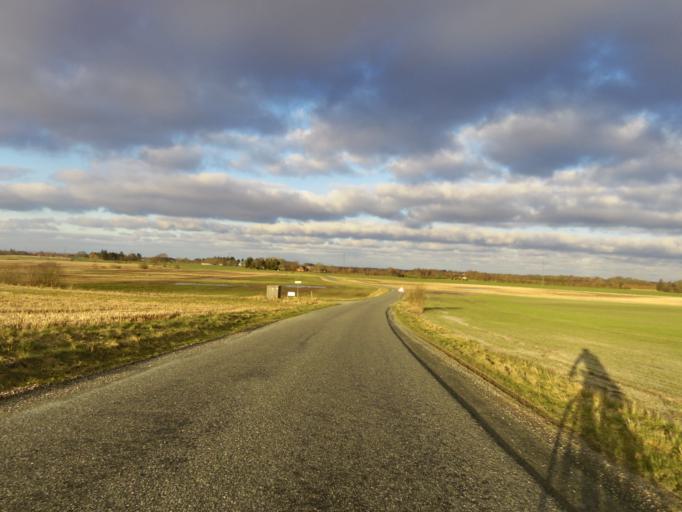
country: DK
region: South Denmark
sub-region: Esbjerg Kommune
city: Ribe
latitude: 55.2856
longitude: 8.8457
